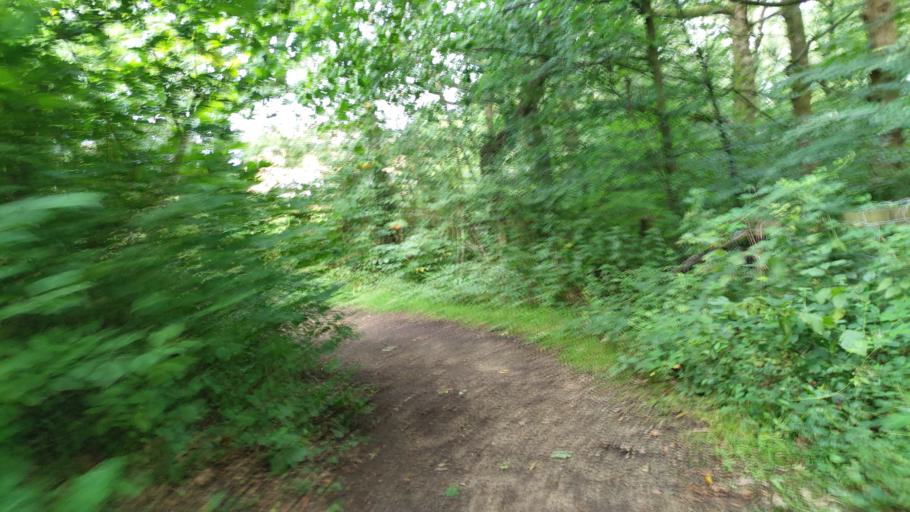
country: GB
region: England
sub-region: Lancashire
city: Chorley
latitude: 53.6329
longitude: -2.6336
